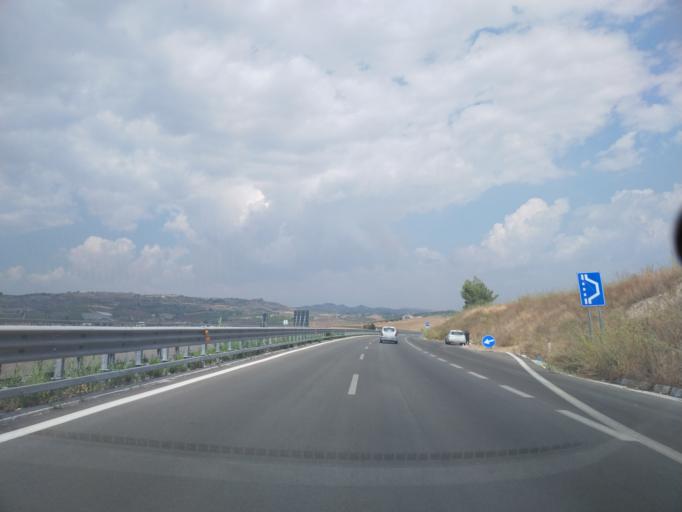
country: IT
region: Sicily
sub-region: Agrigento
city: Favara
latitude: 37.3573
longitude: 13.6834
